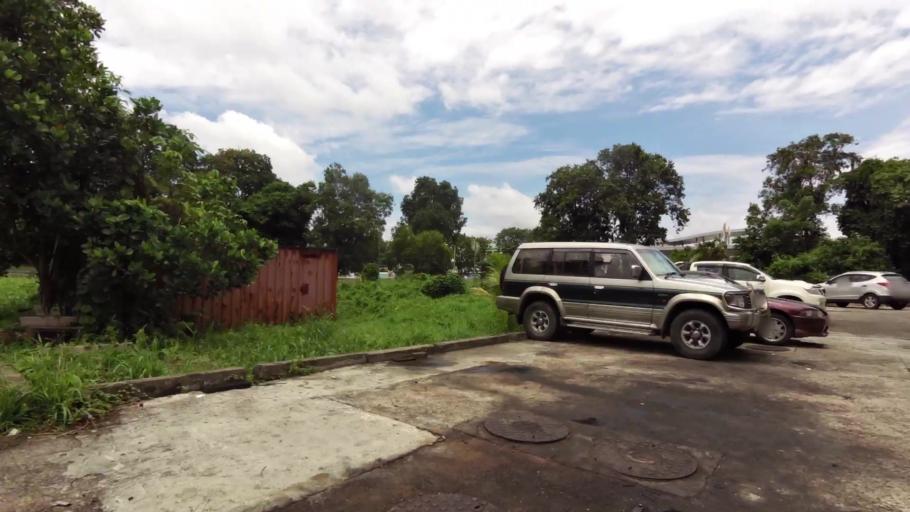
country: BN
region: Brunei and Muara
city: Bandar Seri Begawan
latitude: 4.9107
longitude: 114.9194
